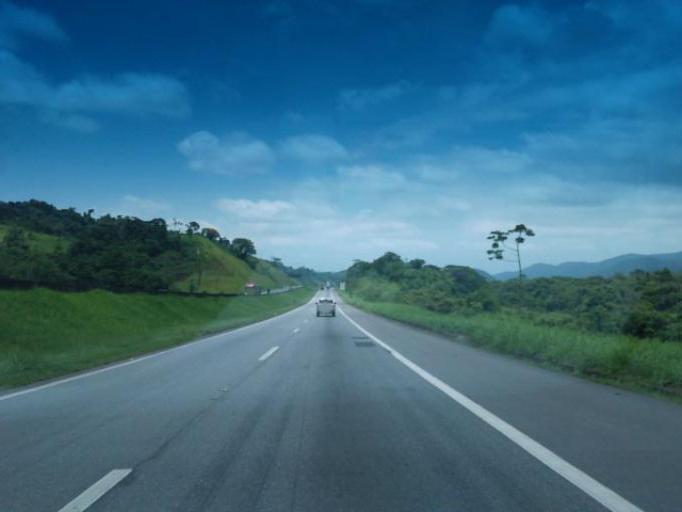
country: BR
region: Sao Paulo
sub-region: Miracatu
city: Miracatu
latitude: -24.1710
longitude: -47.3400
